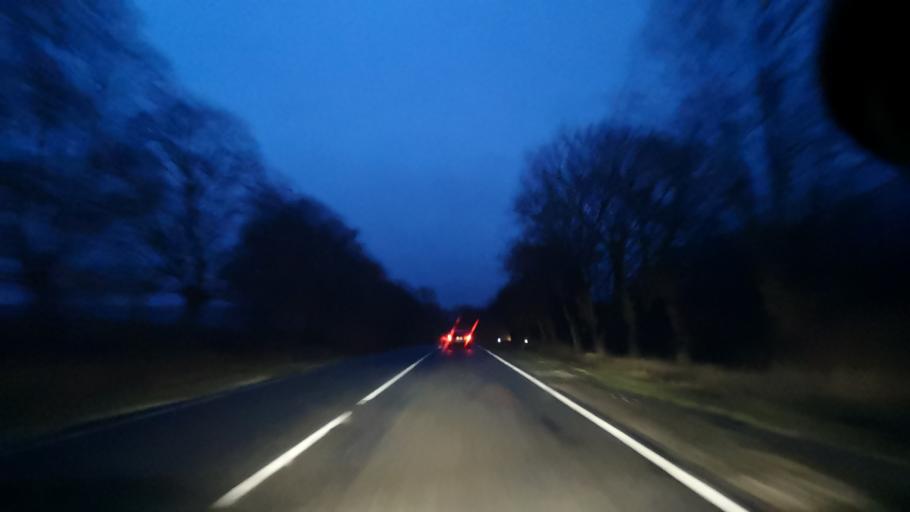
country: MD
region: Orhei
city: Orhei
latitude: 47.4791
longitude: 28.7912
